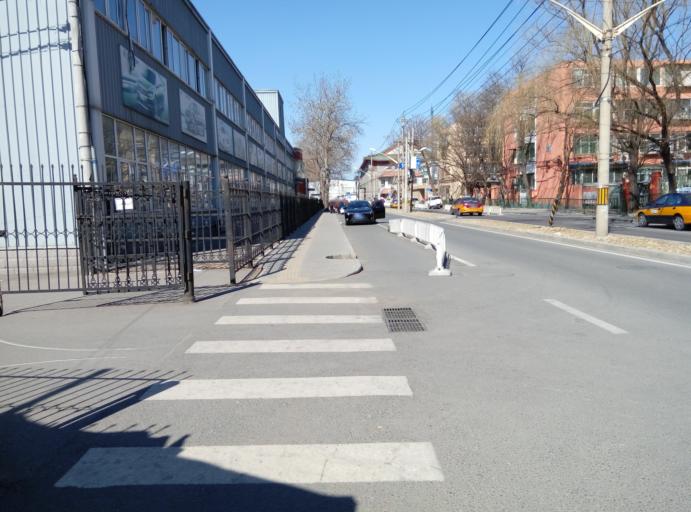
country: CN
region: Beijing
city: Haidian
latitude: 39.9911
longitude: 116.2864
